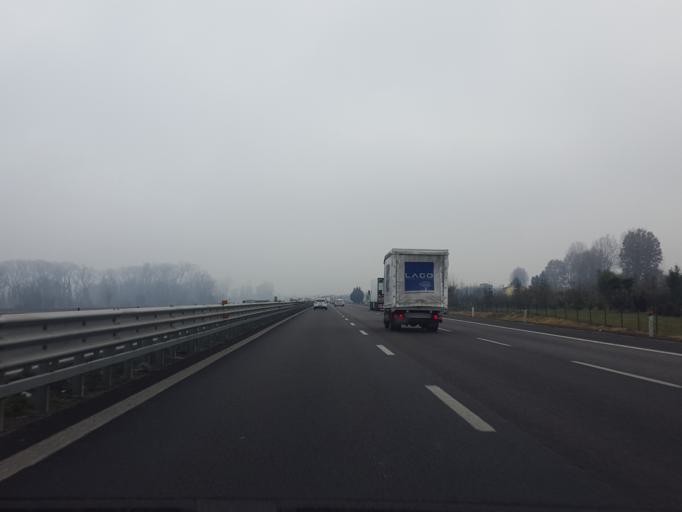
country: IT
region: Veneto
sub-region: Provincia di Vicenza
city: Grumolo delle Abbadesse
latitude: 45.4911
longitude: 11.6672
